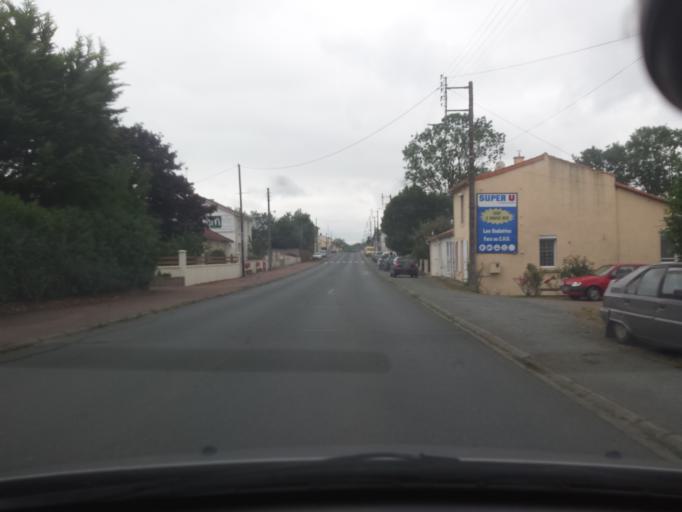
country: FR
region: Pays de la Loire
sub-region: Departement de la Vendee
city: Saint-Florent-des-Bois
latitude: 46.5908
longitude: -1.3115
